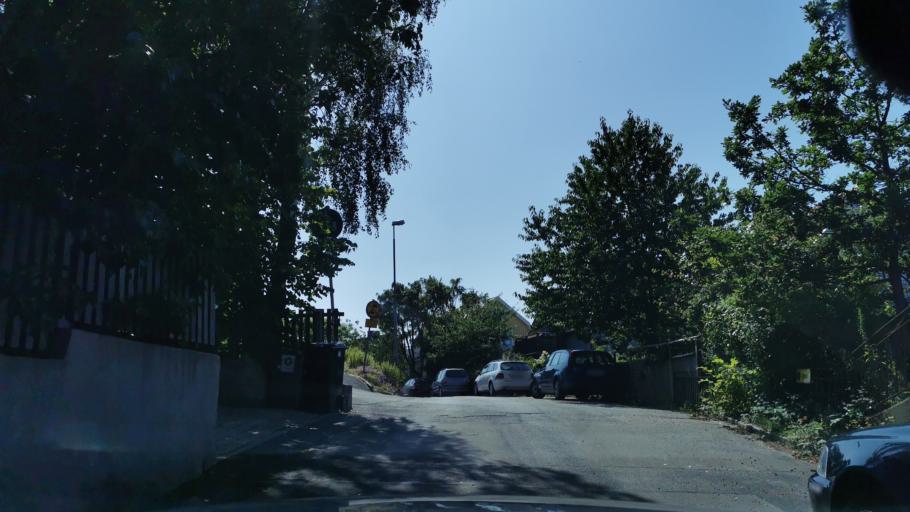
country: SE
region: Vaestra Goetaland
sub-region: Molndal
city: Moelndal
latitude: 57.6783
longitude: 11.9954
